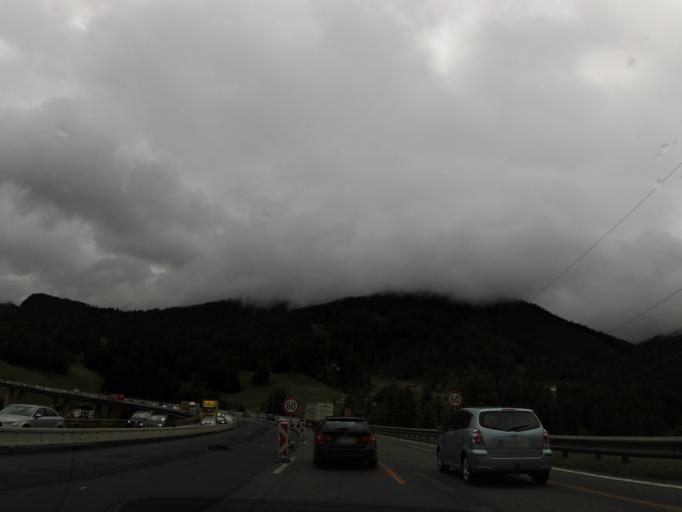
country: AT
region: Tyrol
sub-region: Politischer Bezirk Innsbruck Land
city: Gries am Brenner
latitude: 47.0369
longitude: 11.4740
